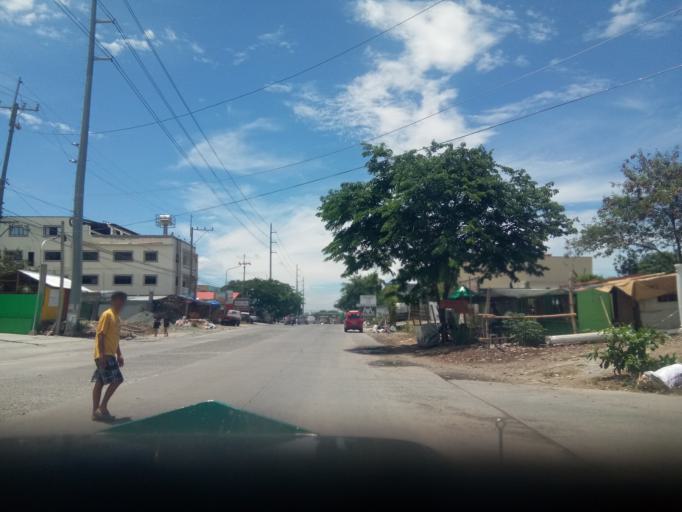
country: PH
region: Calabarzon
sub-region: Province of Cavite
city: Manggahan
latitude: 14.3118
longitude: 120.9158
